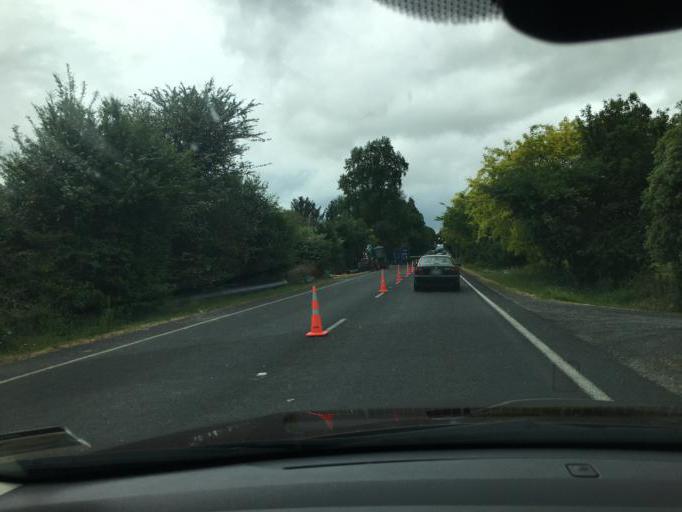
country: NZ
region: Waikato
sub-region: Waipa District
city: Cambridge
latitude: -37.9234
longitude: 175.4352
